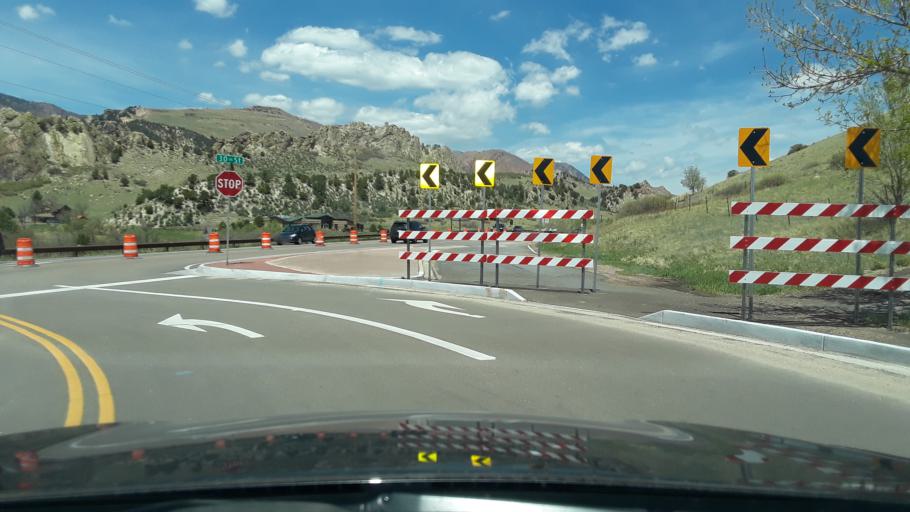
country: US
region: Colorado
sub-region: El Paso County
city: Manitou Springs
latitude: 38.8883
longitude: -104.8747
